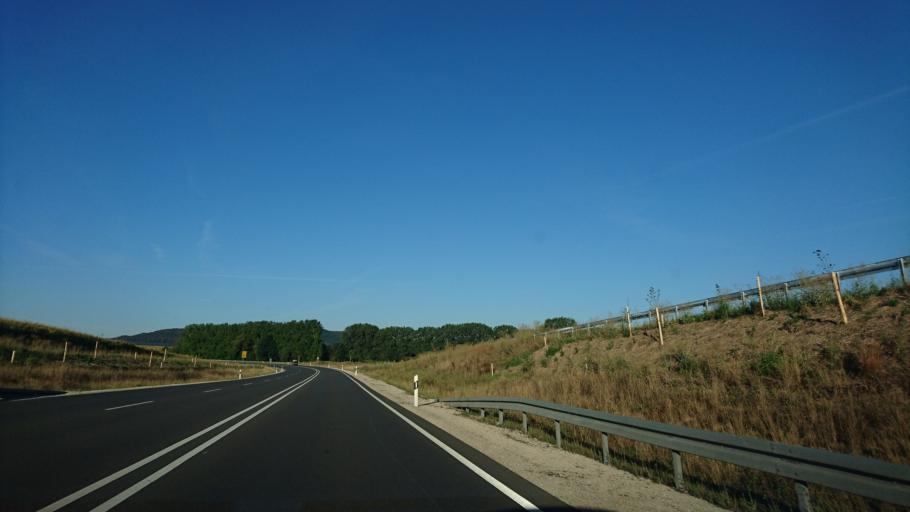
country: DE
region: Bavaria
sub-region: Regierungsbezirk Mittelfranken
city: Weissenburg in Bayern
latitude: 48.9921
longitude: 10.9442
